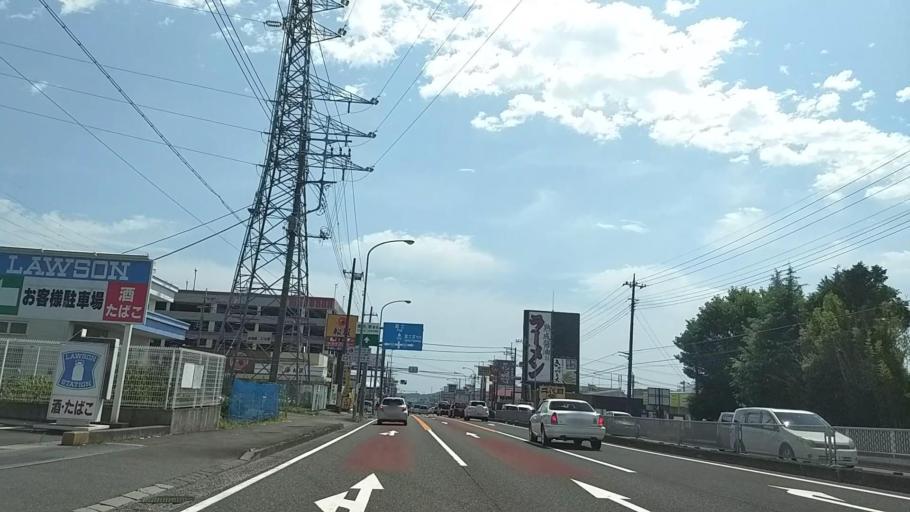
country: JP
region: Shizuoka
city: Fujinomiya
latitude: 35.2415
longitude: 138.6191
